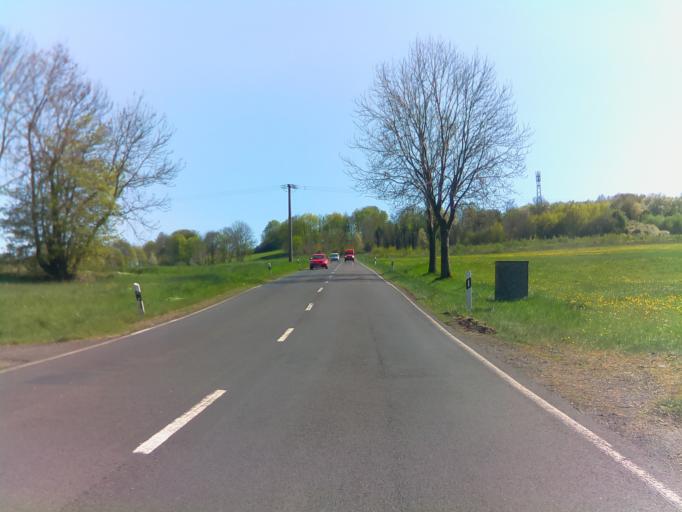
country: DE
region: Hesse
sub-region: Regierungsbezirk Giessen
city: Grebenhain
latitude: 50.5179
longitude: 9.3316
